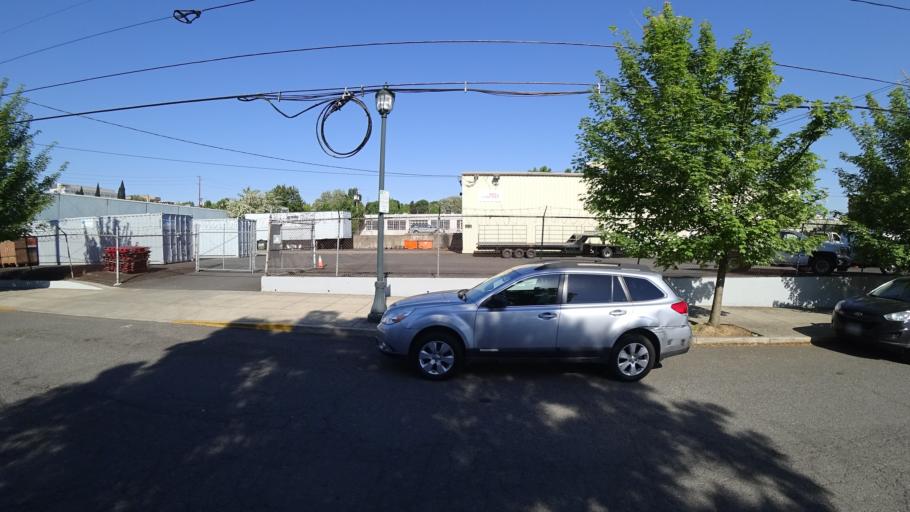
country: US
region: Oregon
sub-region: Multnomah County
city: Portland
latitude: 45.5400
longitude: -122.6749
